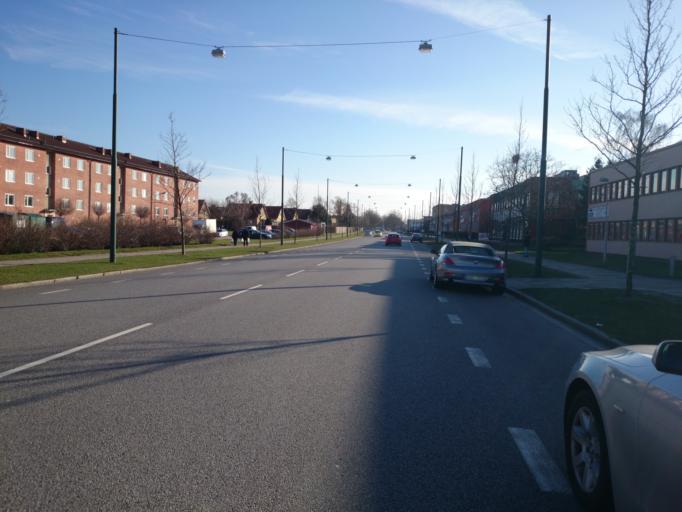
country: SE
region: Skane
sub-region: Malmo
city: Malmoe
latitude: 55.5994
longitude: 13.0386
